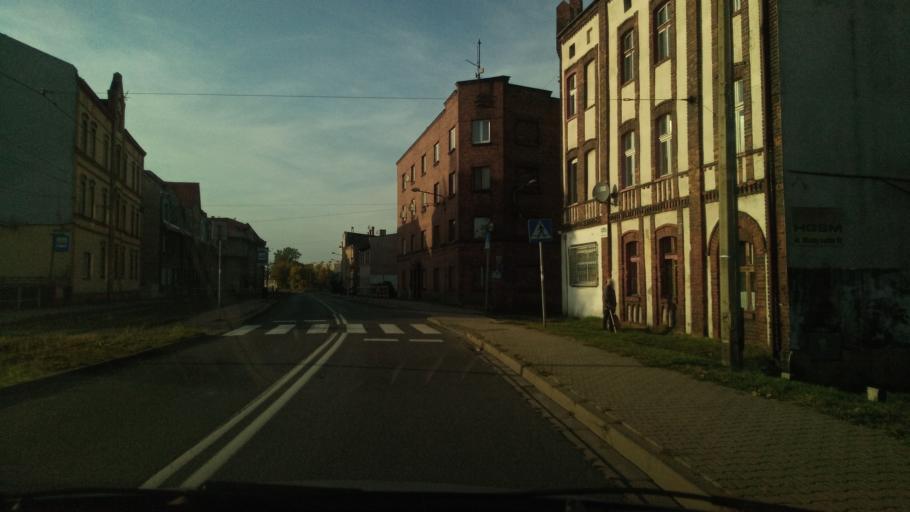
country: PL
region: Silesian Voivodeship
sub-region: Sosnowiec
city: Sosnowiec
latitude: 50.2591
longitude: 19.1124
